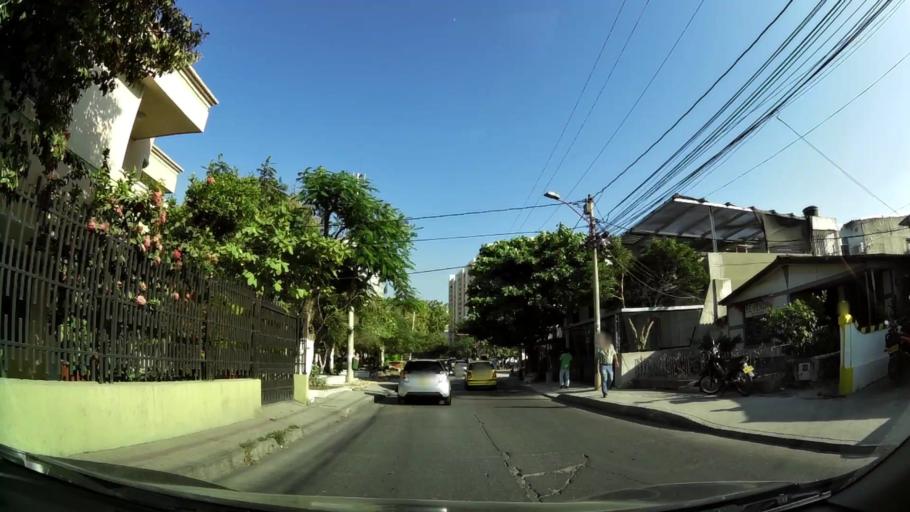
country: CO
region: Bolivar
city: Cartagena
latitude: 10.3897
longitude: -75.4819
